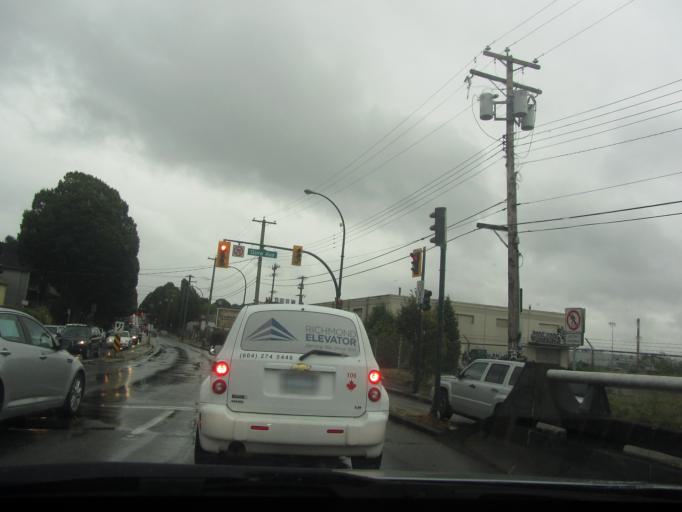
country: CA
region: British Columbia
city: Vancouver
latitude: 49.2767
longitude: -123.0972
